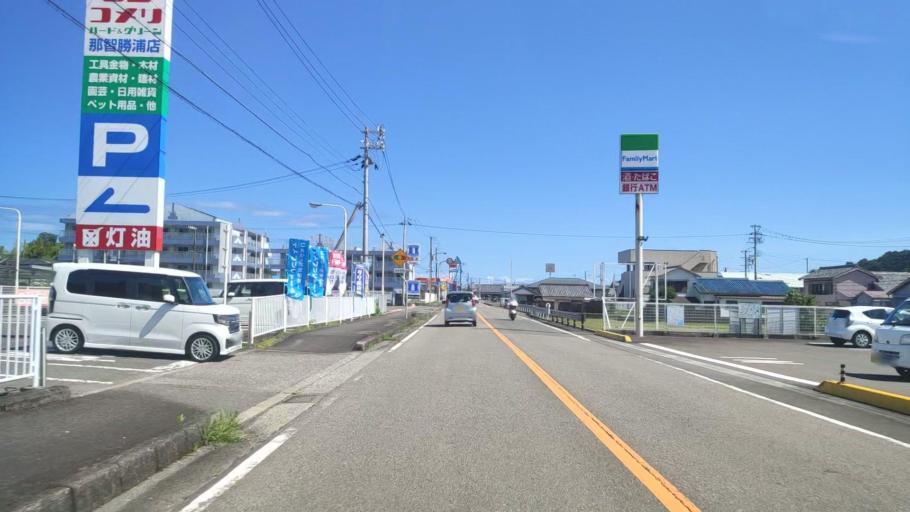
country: JP
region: Wakayama
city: Shingu
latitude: 33.5840
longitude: 135.9195
